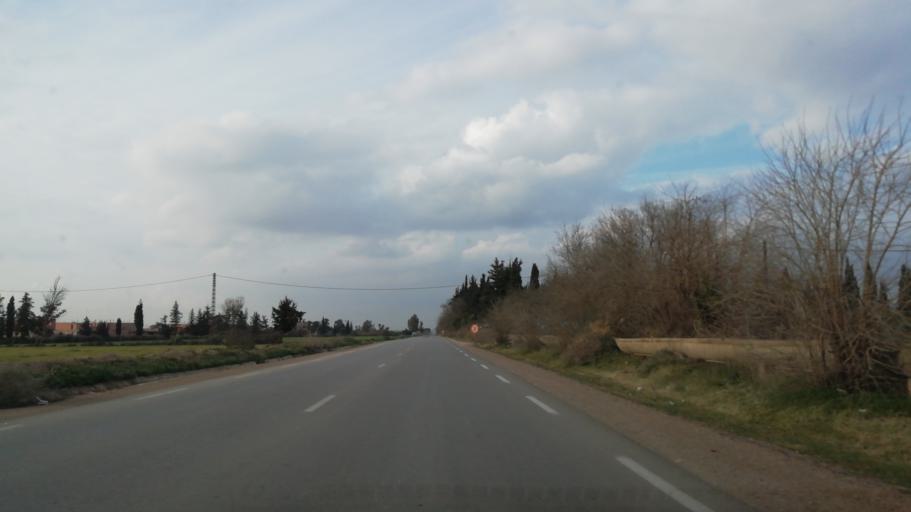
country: DZ
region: Mascara
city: Sig
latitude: 35.6774
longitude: -0.0079
